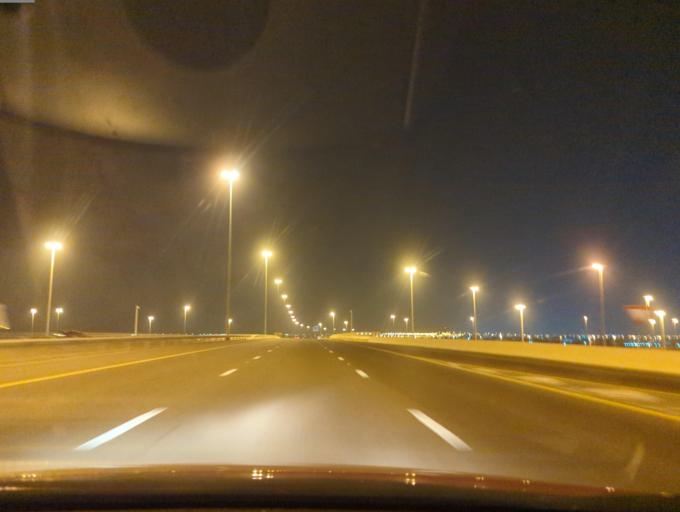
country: AE
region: Abu Dhabi
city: Abu Dhabi
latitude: 24.4207
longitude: 54.7633
